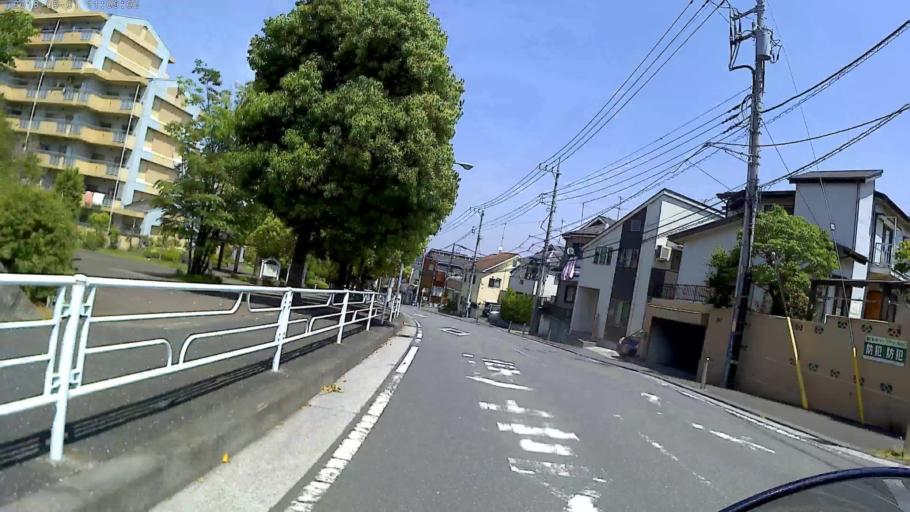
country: JP
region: Kanagawa
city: Minami-rinkan
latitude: 35.4869
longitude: 139.5368
